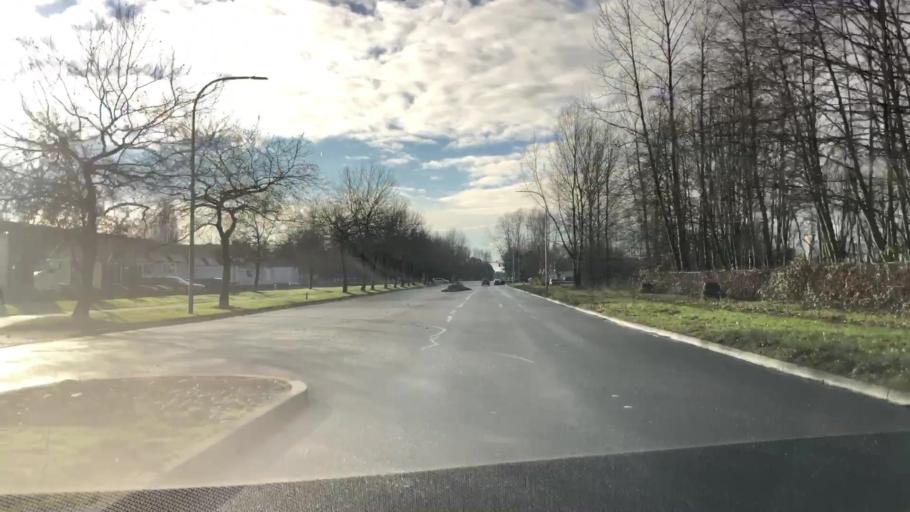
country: US
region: Washington
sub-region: King County
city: Tukwila
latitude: 47.4431
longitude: -122.2329
